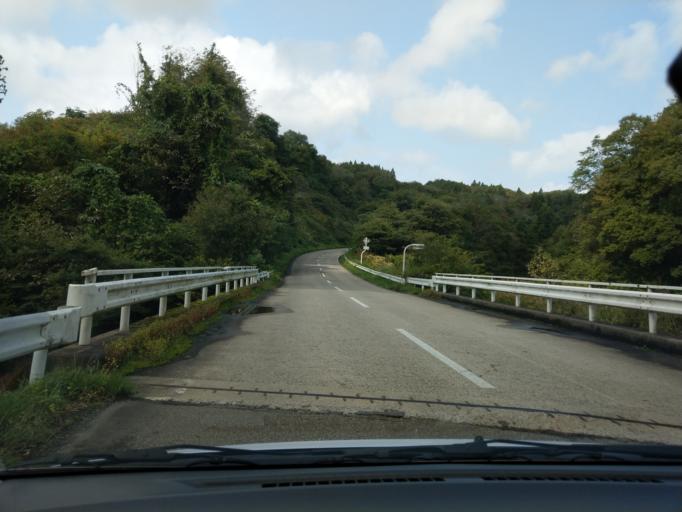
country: JP
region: Akita
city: Omagari
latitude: 39.4734
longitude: 140.3107
